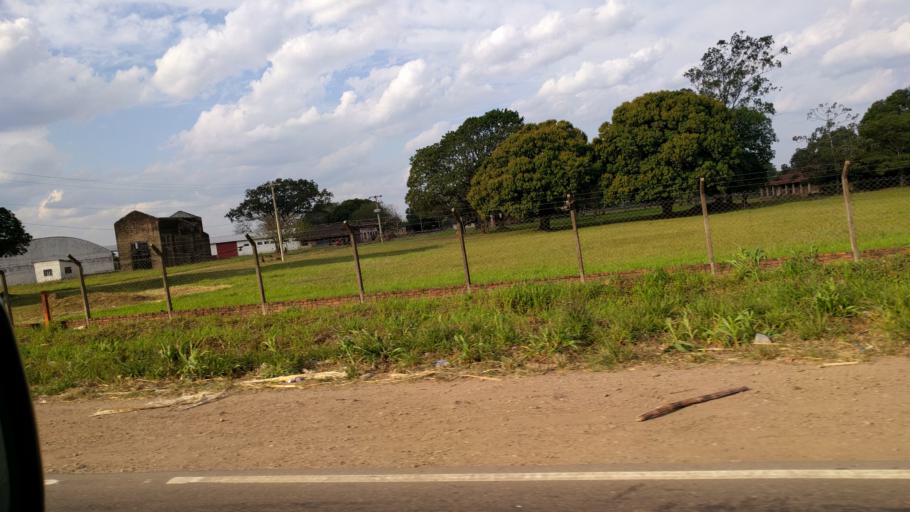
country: BO
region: Santa Cruz
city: Warnes
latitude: -17.5468
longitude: -63.1603
